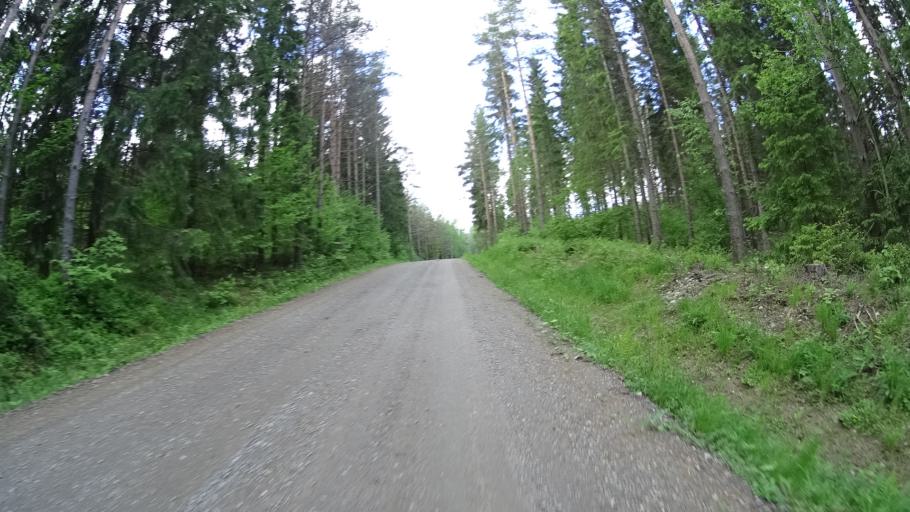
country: FI
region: Uusimaa
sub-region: Raaseporin
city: Pohja
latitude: 60.1669
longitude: 23.6021
